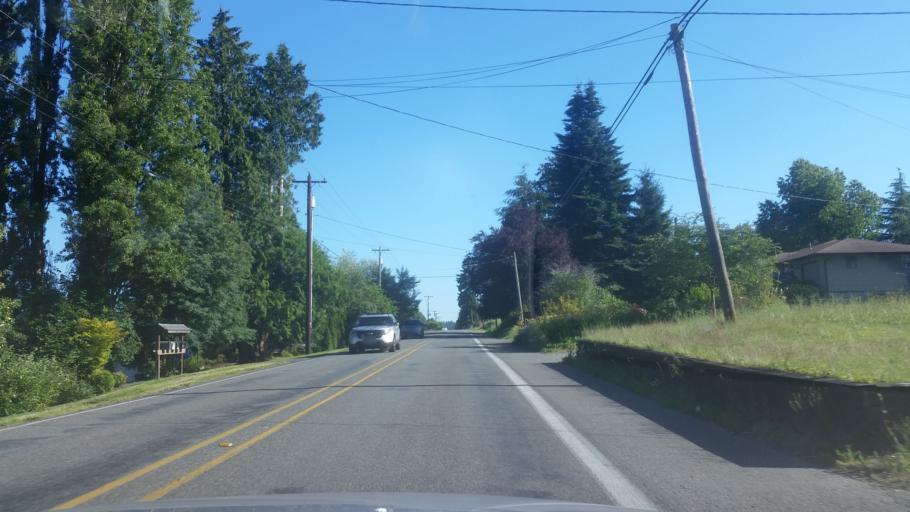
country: US
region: Washington
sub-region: Snohomish County
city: Cathcart
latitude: 47.8635
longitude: -122.0991
